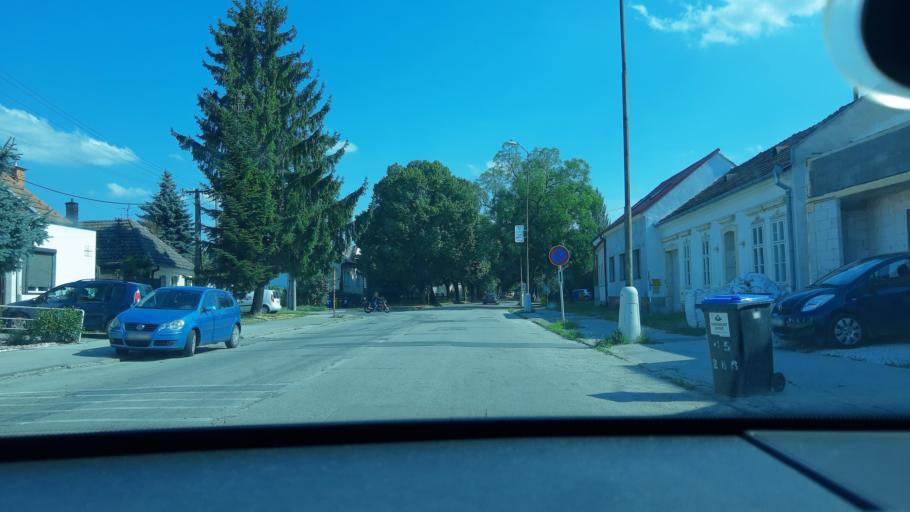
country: SK
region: Trnavsky
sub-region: Okres Trnava
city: Piestany
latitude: 48.5992
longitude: 17.8329
